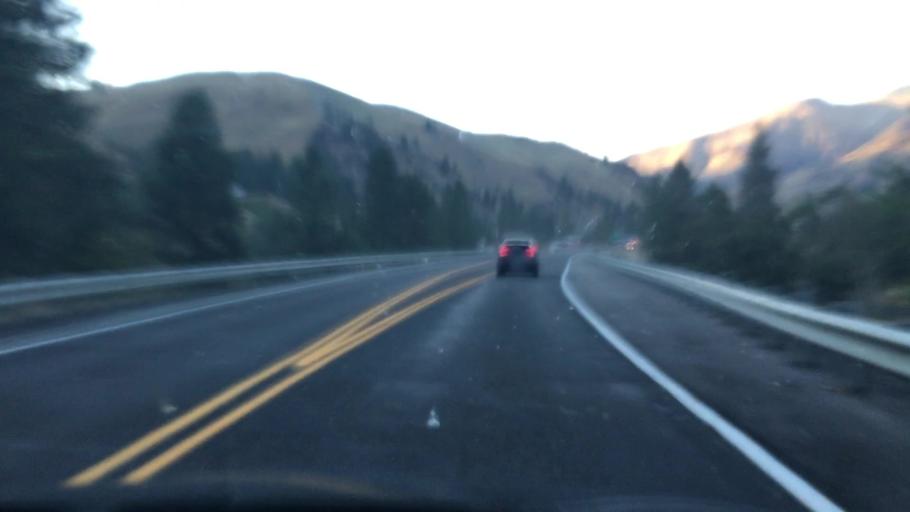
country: US
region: Idaho
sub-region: Valley County
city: McCall
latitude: 45.3059
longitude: -116.3622
